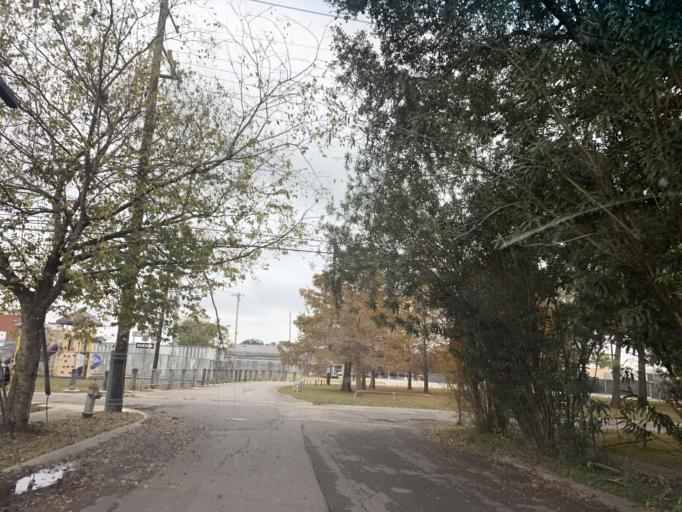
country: US
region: Louisiana
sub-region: Jefferson Parish
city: Metairie
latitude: 29.9880
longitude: -90.1073
